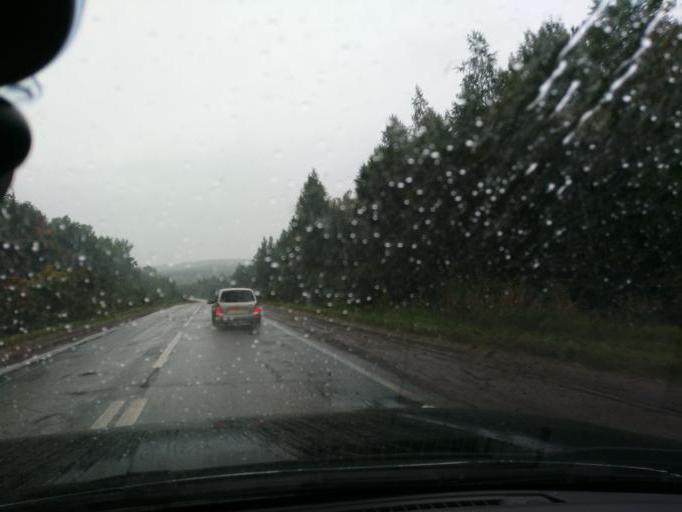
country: RU
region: Perm
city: Barda
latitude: 56.9216
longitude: 55.6803
